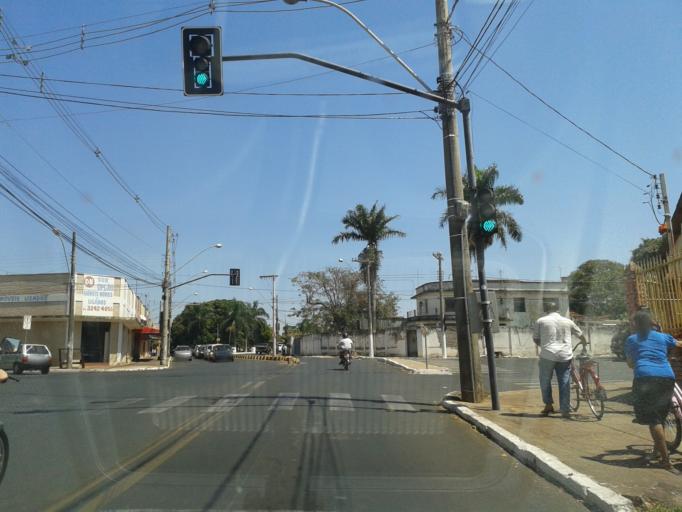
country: BR
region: Minas Gerais
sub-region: Araguari
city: Araguari
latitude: -18.6458
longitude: -48.1977
